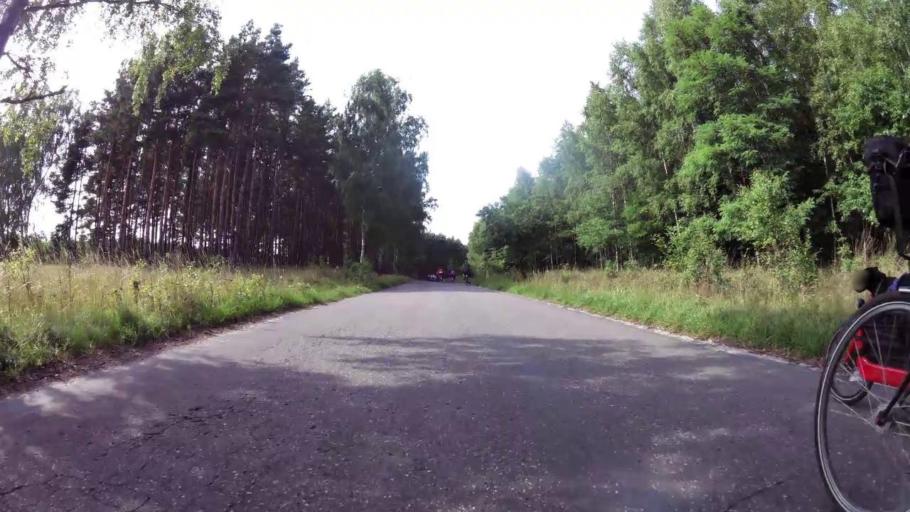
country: PL
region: West Pomeranian Voivodeship
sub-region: Powiat stargardzki
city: Insko
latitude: 53.3802
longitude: 15.5986
